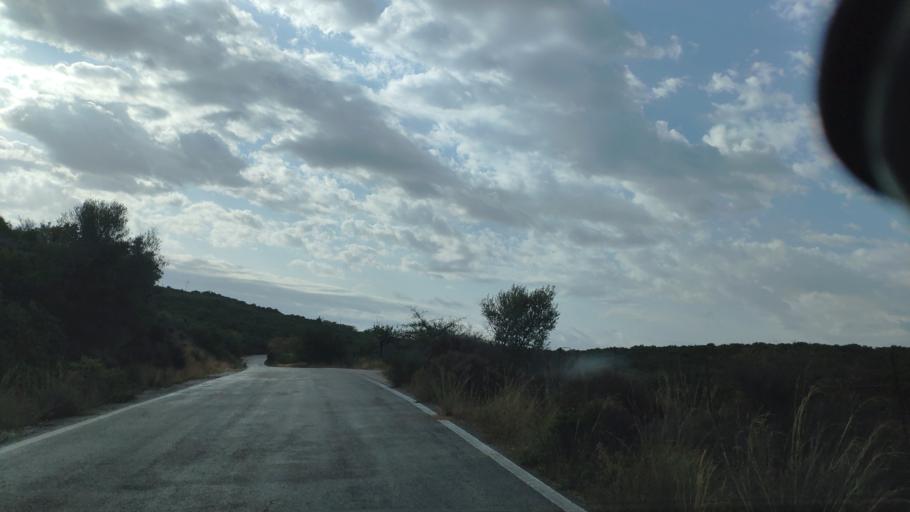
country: GR
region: West Greece
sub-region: Nomos Aitolias kai Akarnanias
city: Sardinia
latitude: 38.8824
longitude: 21.2457
